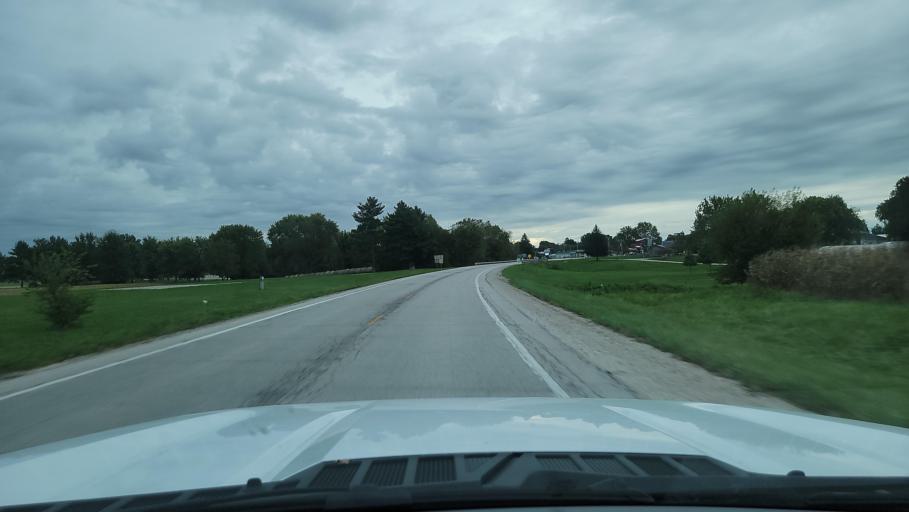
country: US
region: Illinois
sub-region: Schuyler County
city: Rushville
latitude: 40.1167
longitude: -90.5824
